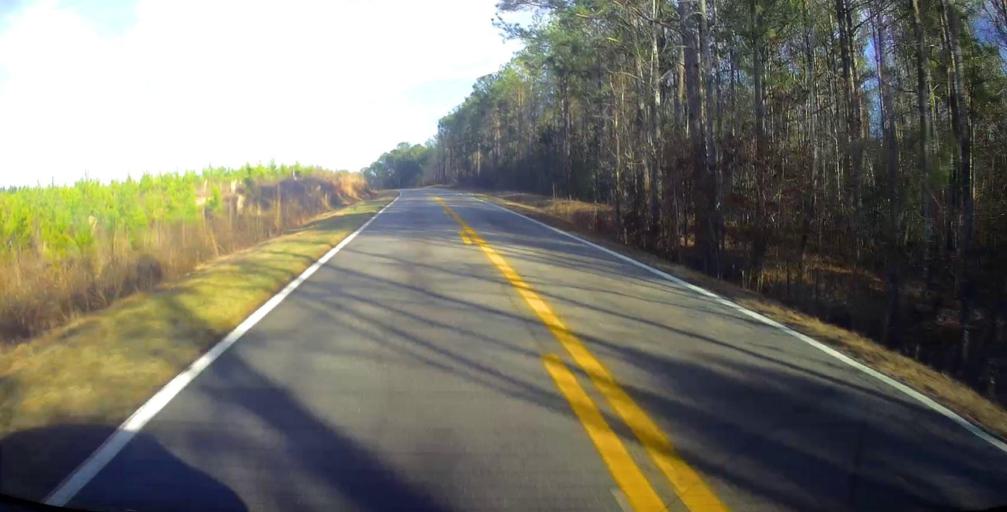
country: US
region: Georgia
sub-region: Crawford County
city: Roberta
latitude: 32.7711
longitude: -84.1067
